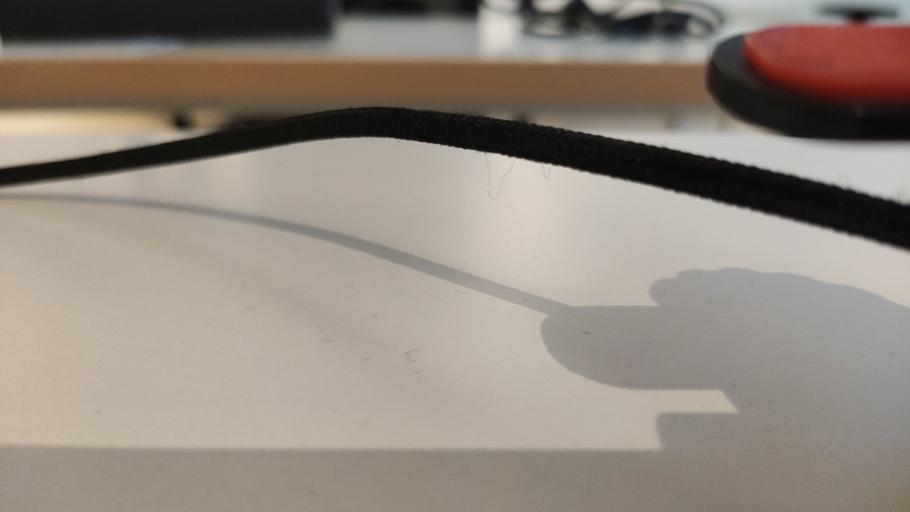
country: RU
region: Moskovskaya
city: Ruza
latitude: 55.7894
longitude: 36.2813
